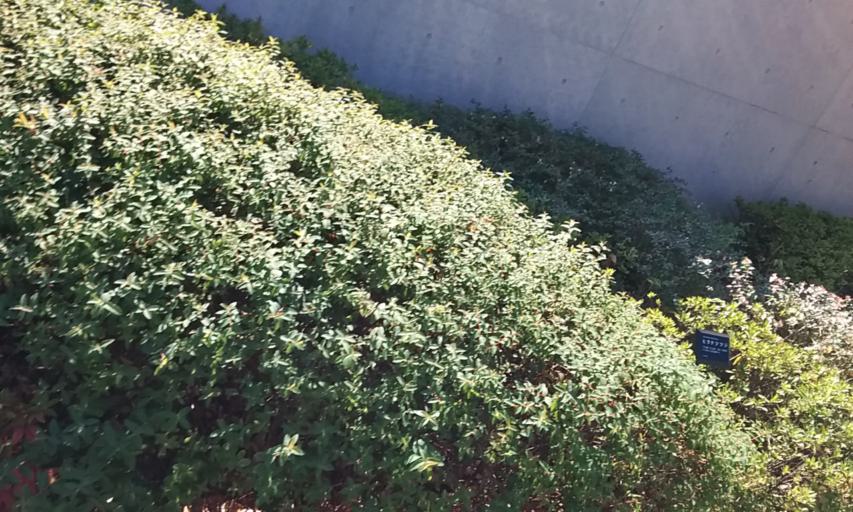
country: JP
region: Tokyo
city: Mitaka-shi
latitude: 35.6620
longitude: 139.5812
